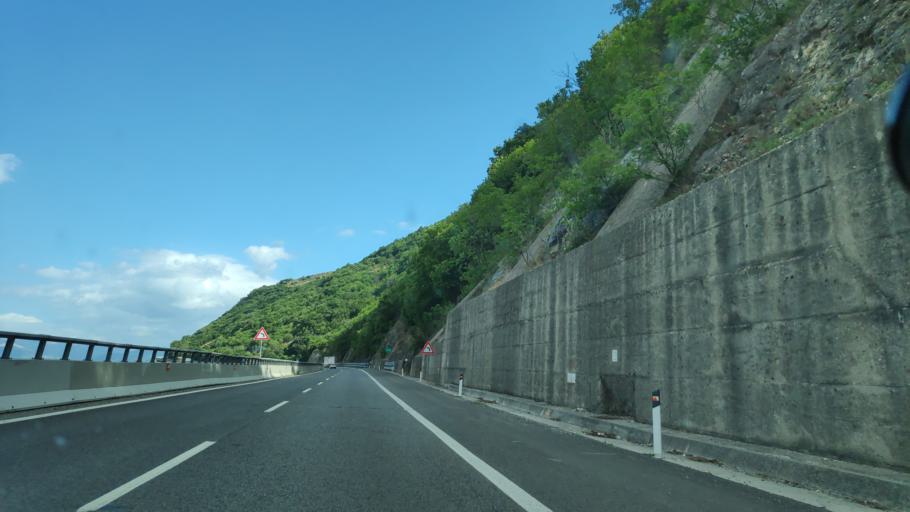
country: IT
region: Campania
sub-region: Provincia di Salerno
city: Sicignano degli Alburni
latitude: 40.5946
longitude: 15.3226
